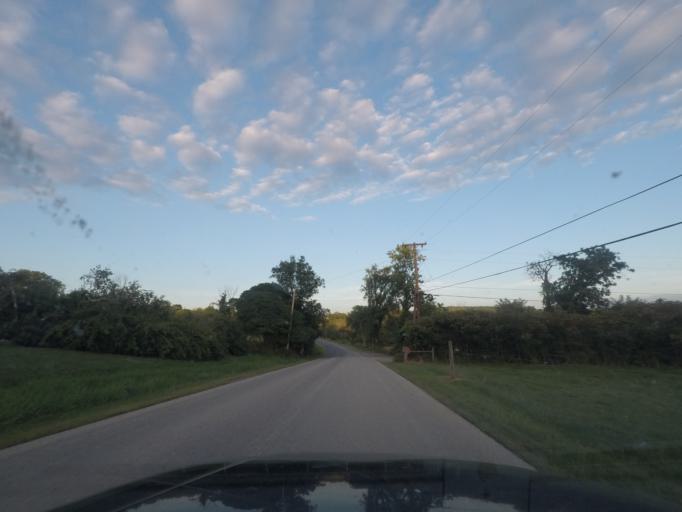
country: US
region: New York
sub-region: Rensselaer County
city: Nassau
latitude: 42.4912
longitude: -73.5702
